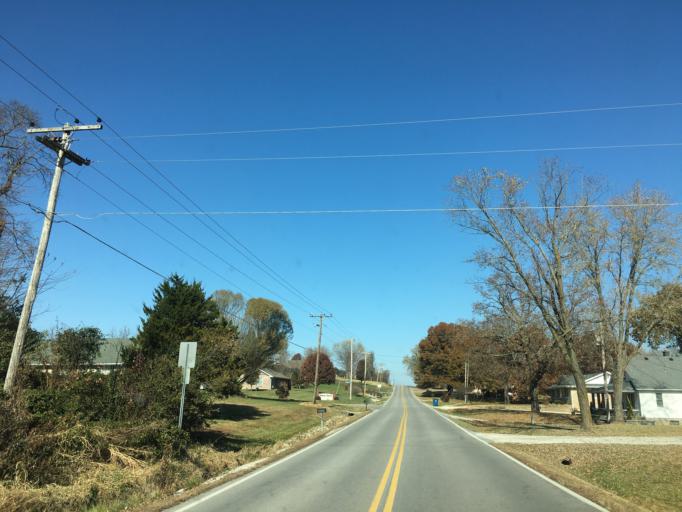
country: US
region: Missouri
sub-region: Cole County
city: Wardsville
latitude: 38.5075
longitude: -92.1755
